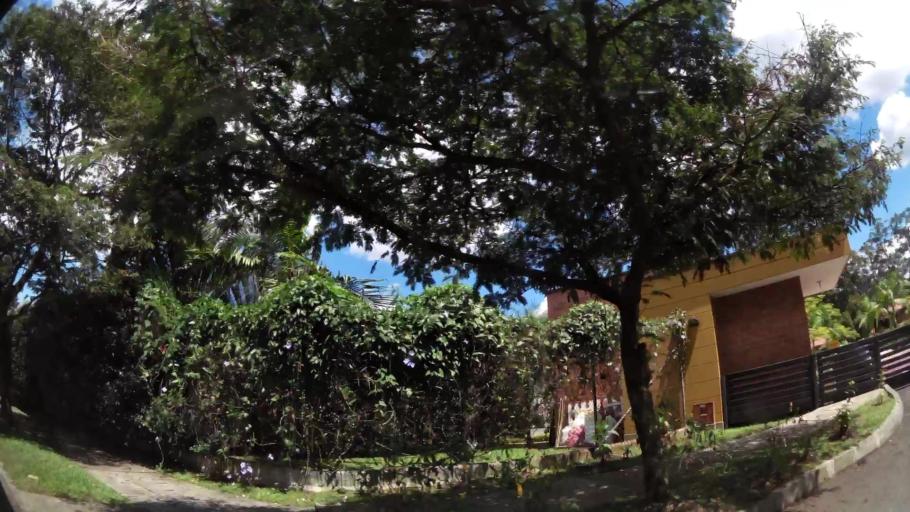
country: CO
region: Antioquia
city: Sabaneta
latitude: 6.1563
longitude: -75.6276
